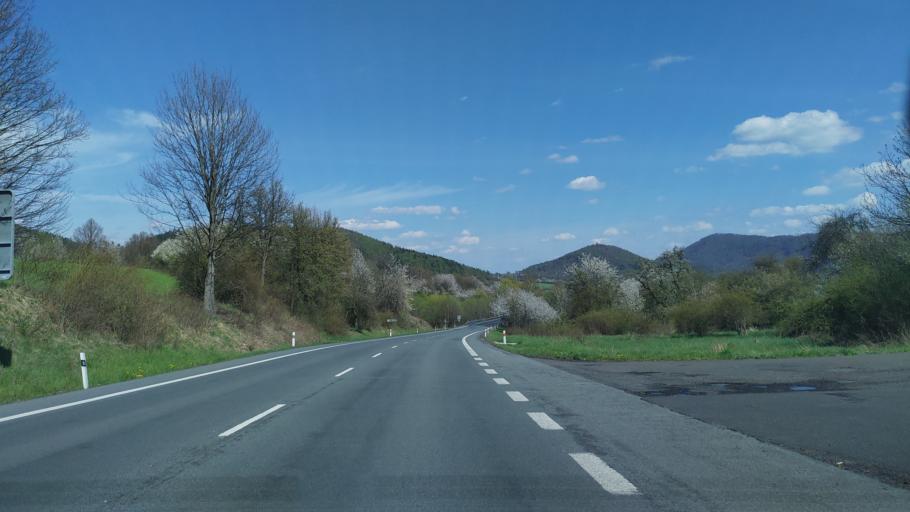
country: CZ
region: Ustecky
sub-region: Okres Chomutov
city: Perstejn
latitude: 50.3746
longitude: 13.1018
